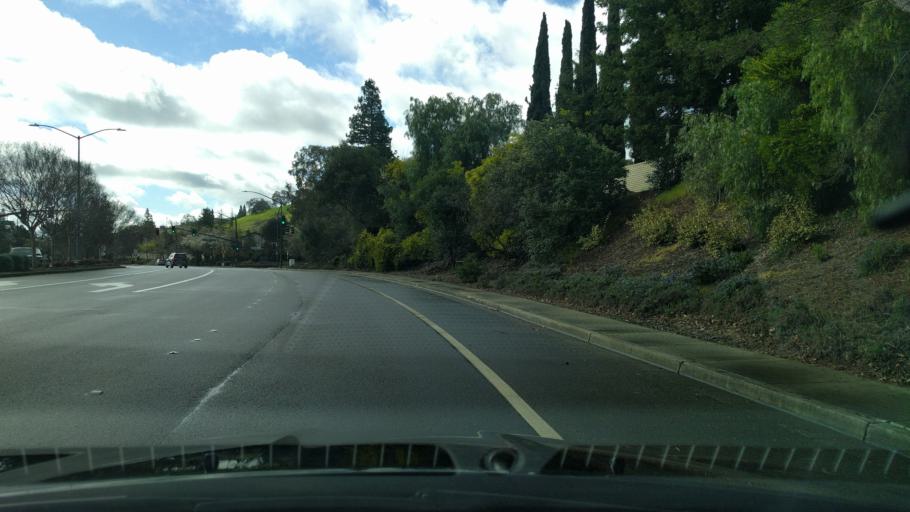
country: US
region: California
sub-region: Contra Costa County
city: San Ramon
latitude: 37.7604
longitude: -121.9684
